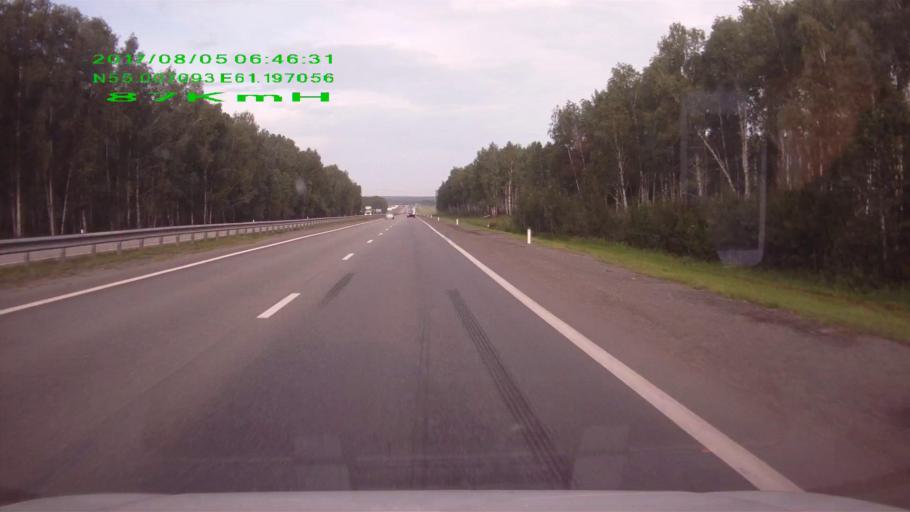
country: RU
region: Chelyabinsk
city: Sargazy
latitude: 55.0071
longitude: 61.1967
